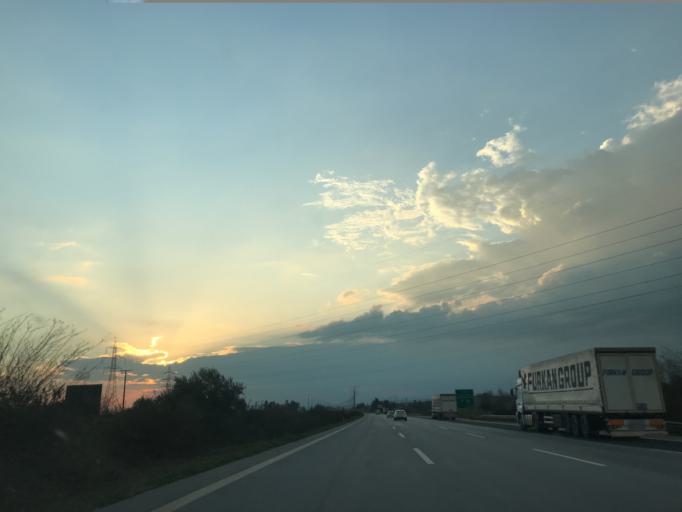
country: TR
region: Mersin
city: Yenice
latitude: 37.0234
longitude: 35.0746
